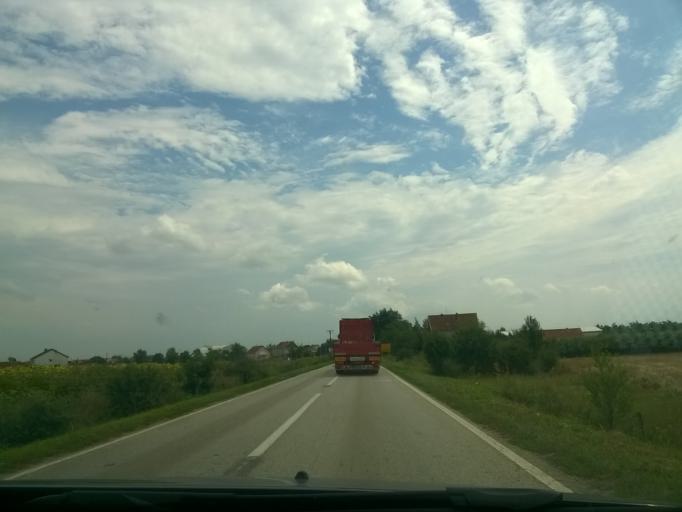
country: RS
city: Lazarevo
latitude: 45.3882
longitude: 20.5229
